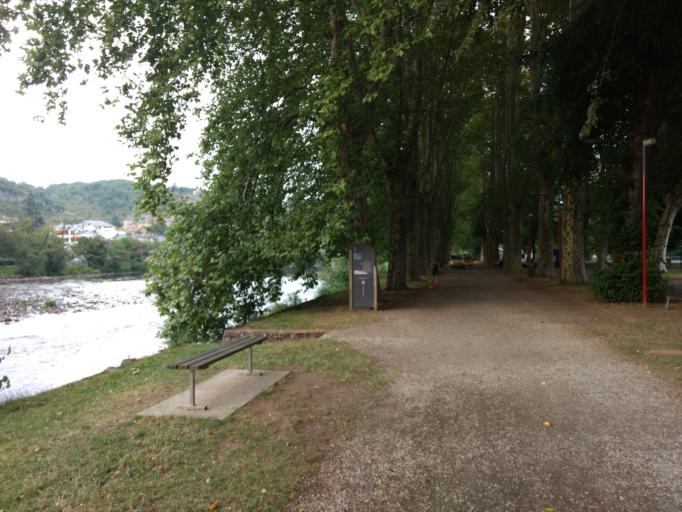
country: FR
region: Midi-Pyrenees
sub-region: Departement de l'Aveyron
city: Espalion
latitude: 44.5214
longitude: 2.7661
